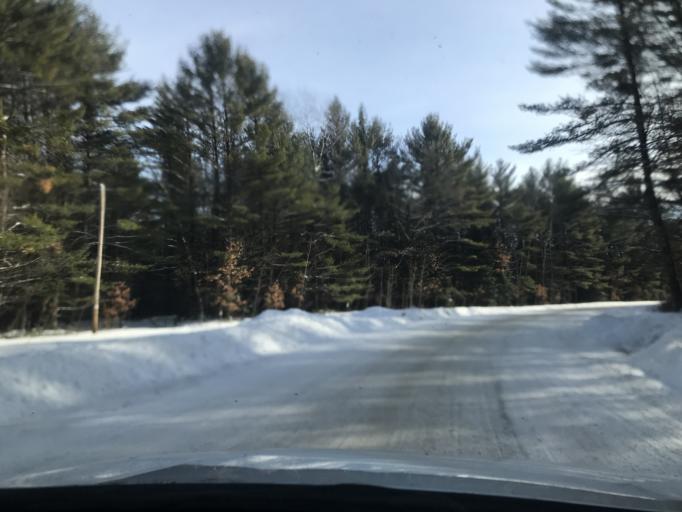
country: US
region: Wisconsin
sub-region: Oconto County
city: Gillett
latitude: 45.1366
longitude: -88.2501
